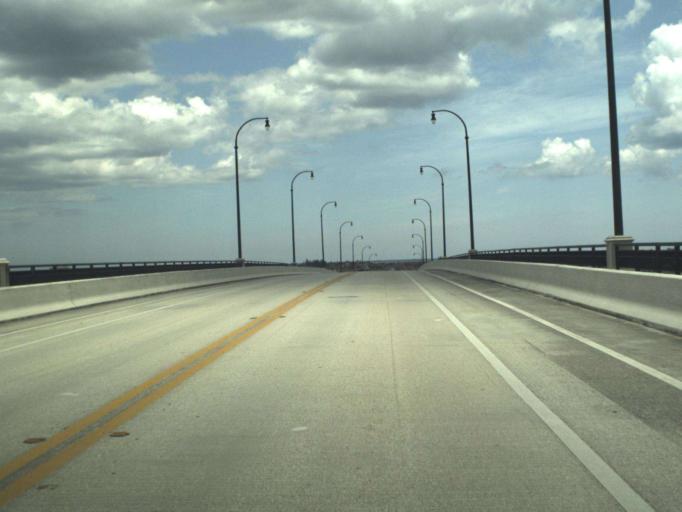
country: US
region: Florida
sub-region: Martin County
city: Jensen Beach
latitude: 27.2533
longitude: -80.2195
